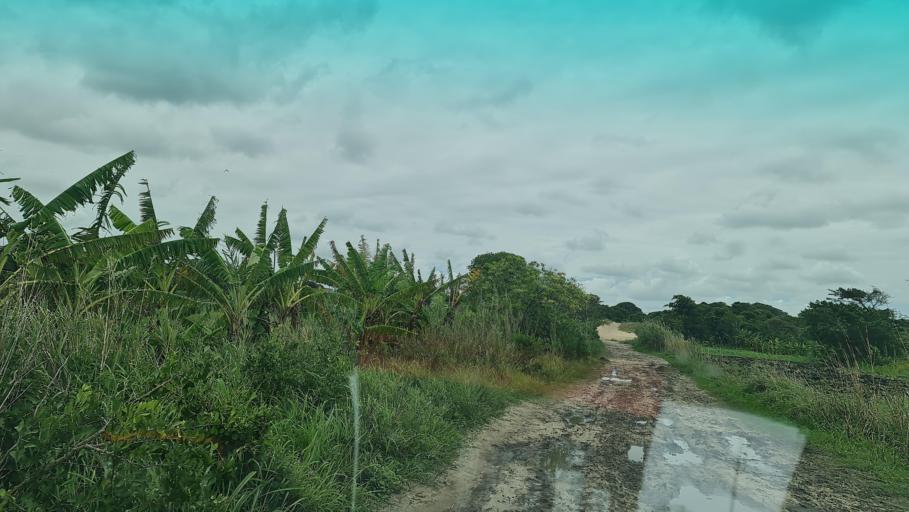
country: MZ
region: Maputo City
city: Maputo
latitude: -25.6990
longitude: 32.7053
